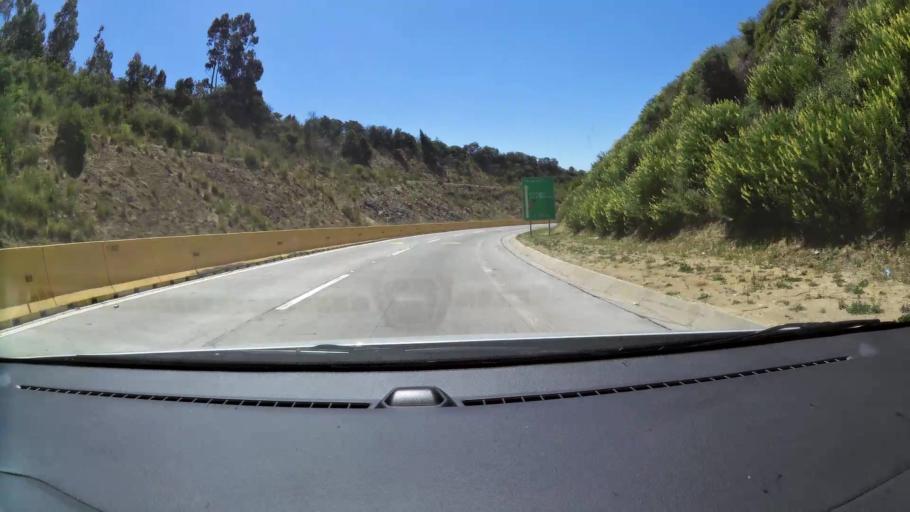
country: CL
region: Valparaiso
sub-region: Provincia de Valparaiso
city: Valparaiso
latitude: -33.0665
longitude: -71.6420
